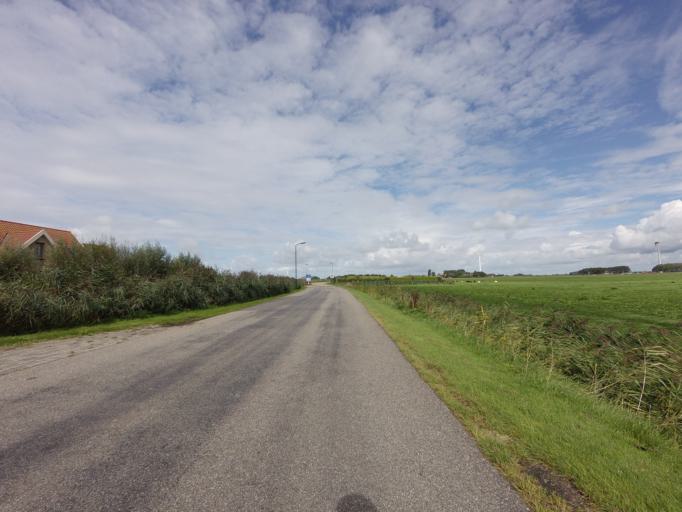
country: NL
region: Friesland
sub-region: Sudwest Fryslan
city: Makkum
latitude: 53.0857
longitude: 5.4225
